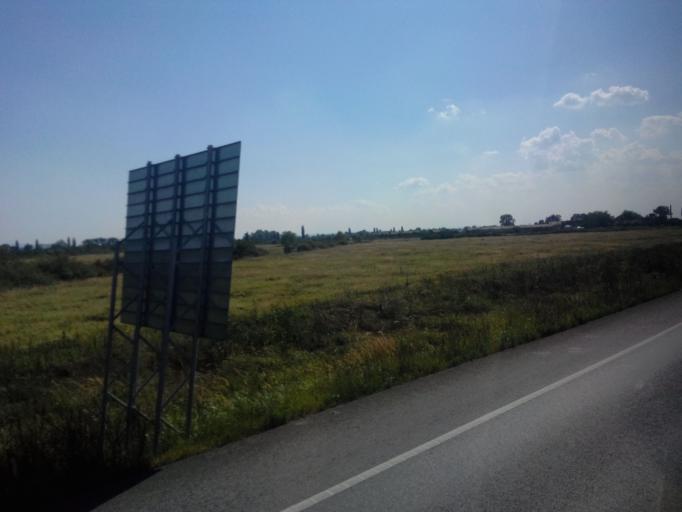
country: RO
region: Timis
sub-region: Municipiul Lugoj
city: Lugoj
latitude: 45.7220
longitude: 21.8906
